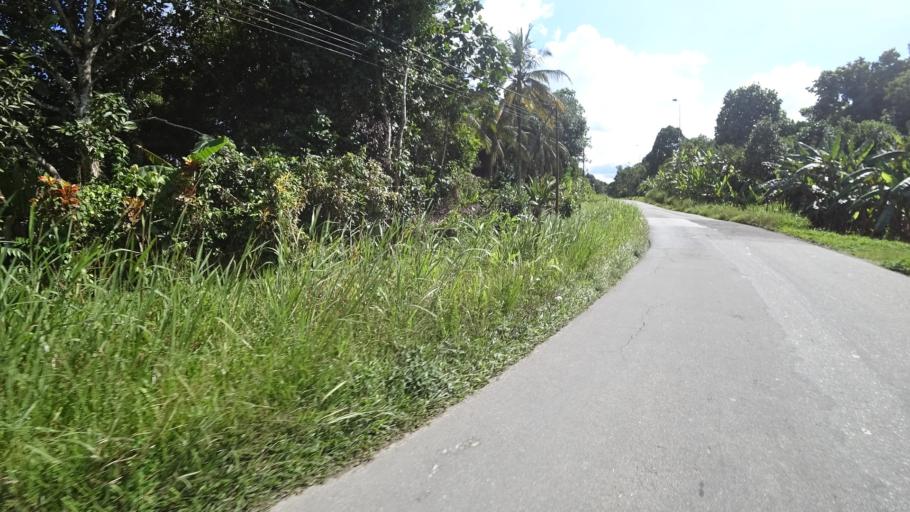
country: BN
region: Tutong
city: Tutong
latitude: 4.7623
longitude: 114.7942
